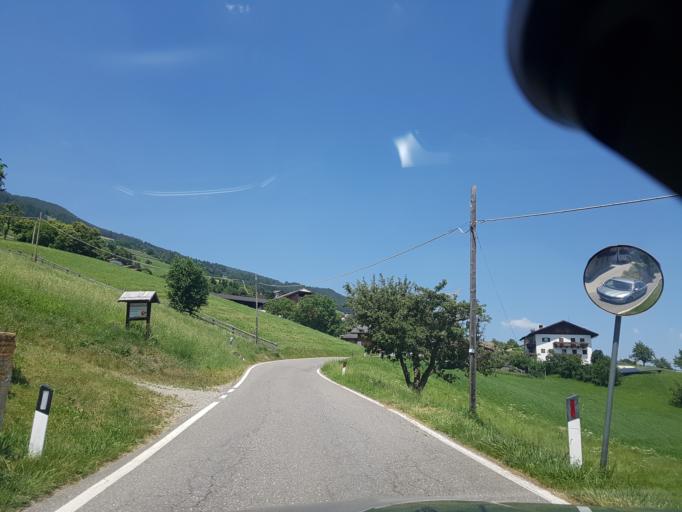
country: IT
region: Trentino-Alto Adige
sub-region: Bolzano
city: Villandro - Villanders
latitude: 46.6265
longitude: 11.5310
